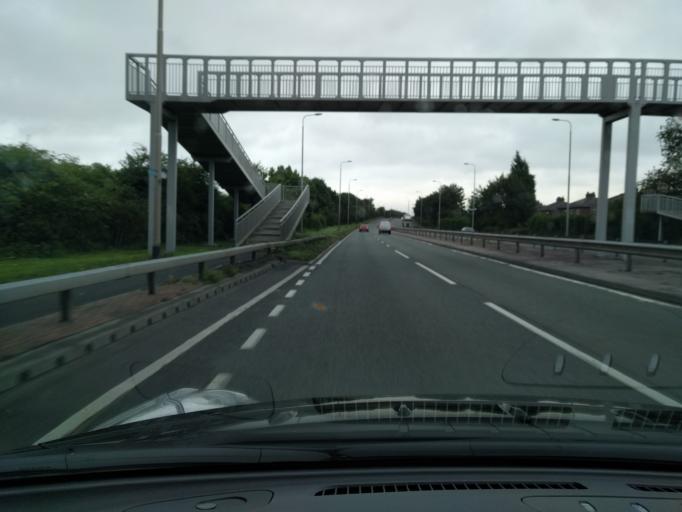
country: GB
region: England
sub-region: Borough of Wigan
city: Ashton in Makerfield
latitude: 53.4727
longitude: -2.6533
